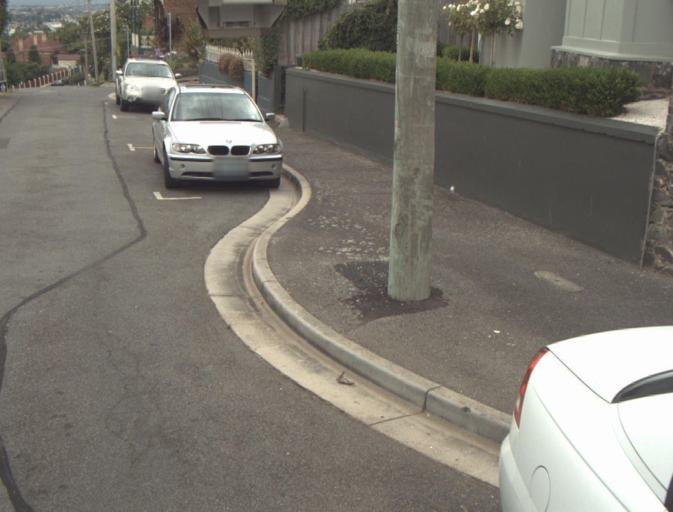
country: AU
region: Tasmania
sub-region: Launceston
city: East Launceston
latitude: -41.4394
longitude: 147.1449
